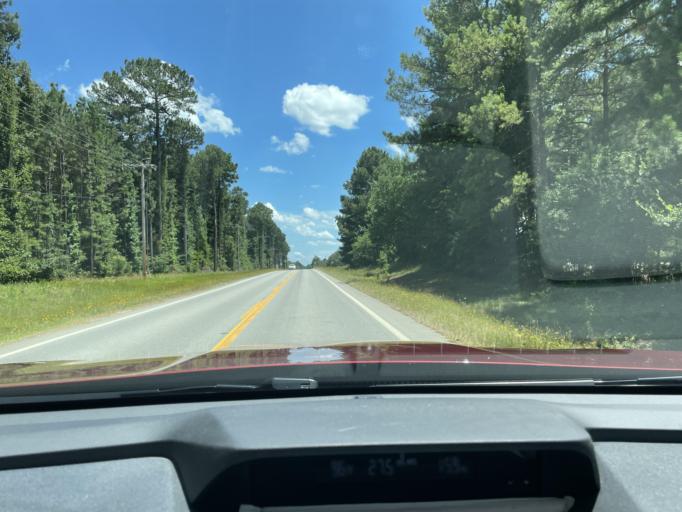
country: US
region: Arkansas
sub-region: Drew County
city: Monticello
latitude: 33.6254
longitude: -91.7536
